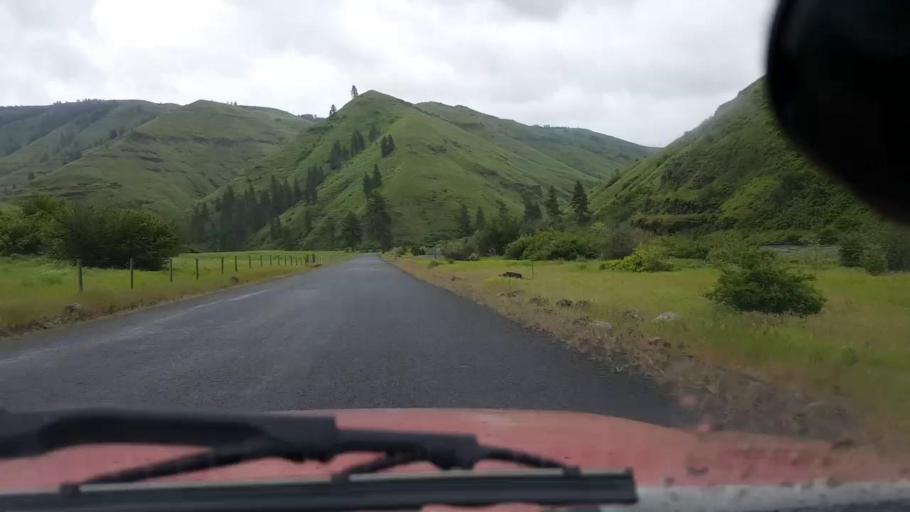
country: US
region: Washington
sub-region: Asotin County
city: Asotin
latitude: 46.0318
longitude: -117.3178
